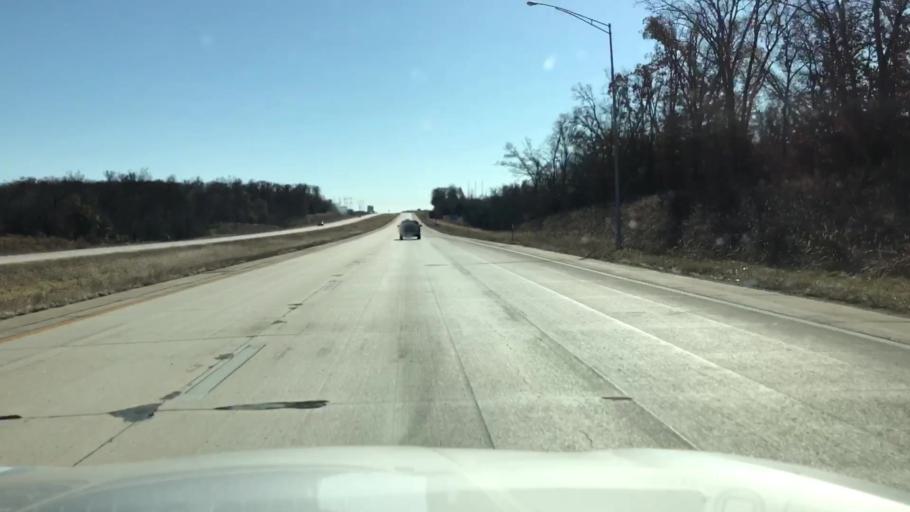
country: US
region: Missouri
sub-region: Jasper County
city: Duenweg
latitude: 37.0492
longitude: -94.4273
